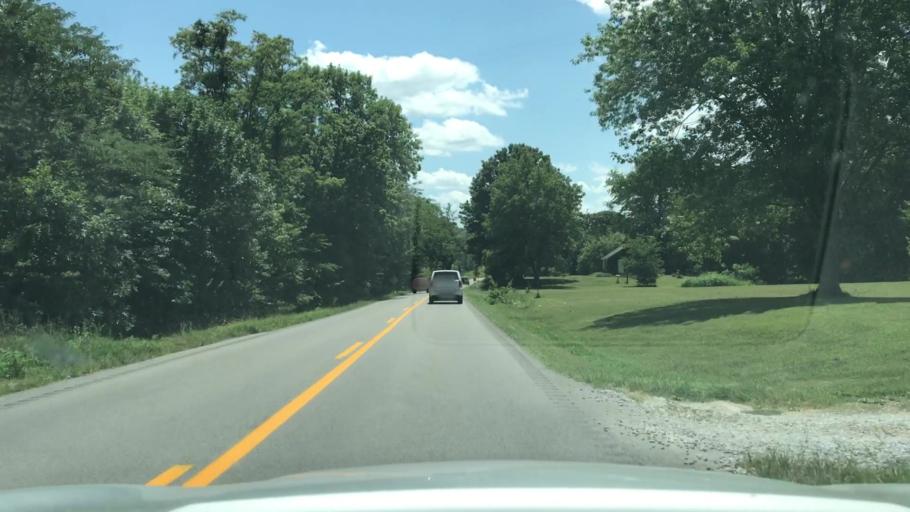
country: US
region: Kentucky
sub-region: Christian County
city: Hopkinsville
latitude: 36.8921
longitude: -87.4532
